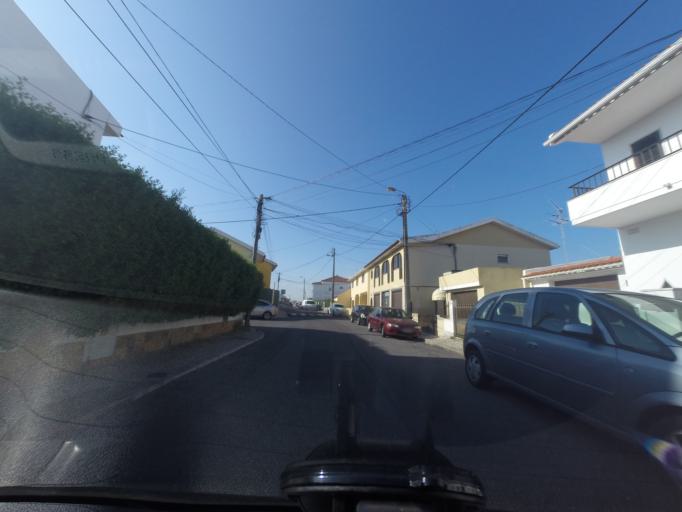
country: PT
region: Lisbon
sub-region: Cascais
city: Sao Domingos de Rana
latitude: 38.7056
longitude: -9.3428
